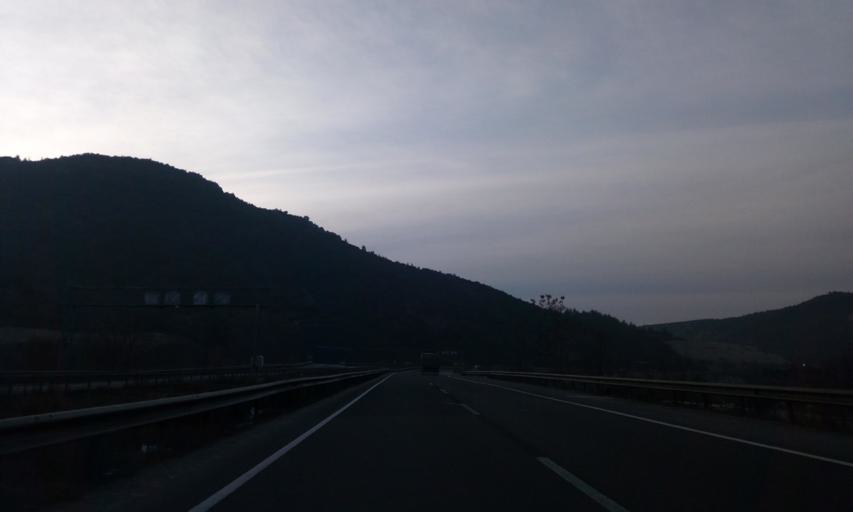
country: TR
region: Bilecik
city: Bilecik
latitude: 40.1662
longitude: 30.0203
